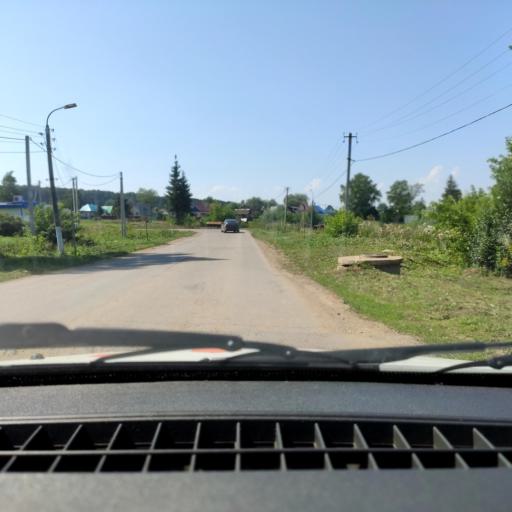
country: RU
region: Bashkortostan
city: Kudeyevskiy
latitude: 54.8691
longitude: 56.7419
